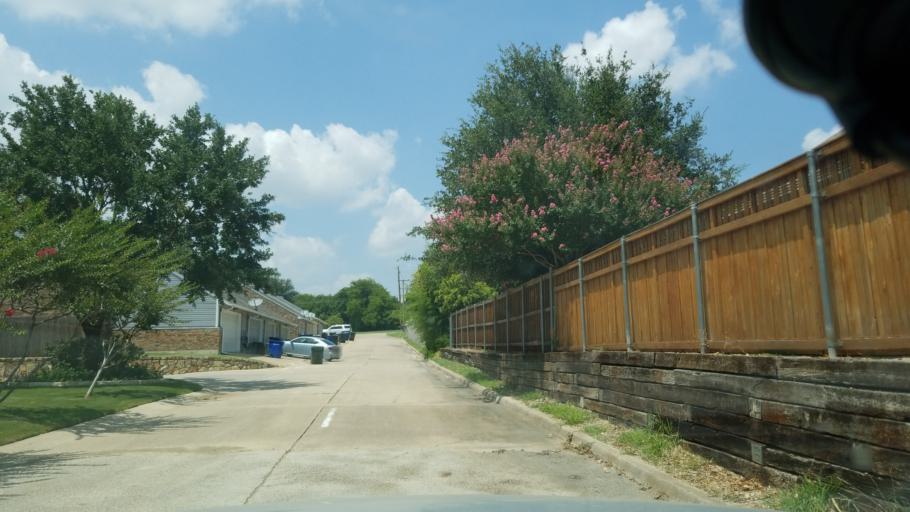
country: US
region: Texas
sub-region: Dallas County
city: Addison
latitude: 32.9689
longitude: -96.8589
